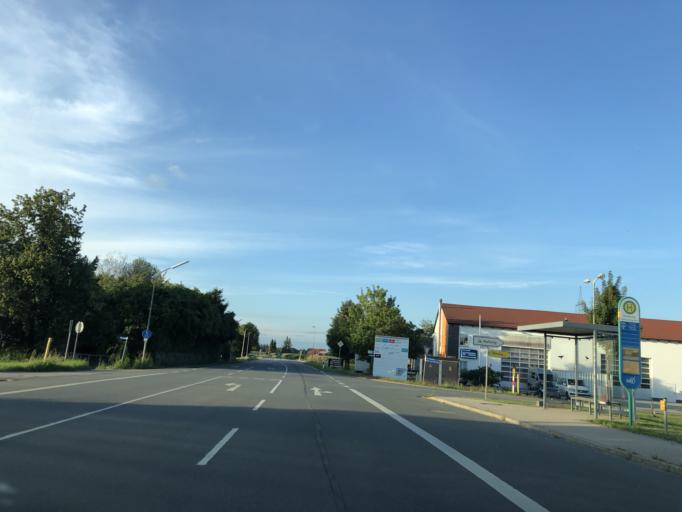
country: DE
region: Bavaria
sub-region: Upper Bavaria
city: Finsing
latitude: 48.2292
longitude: 11.8137
